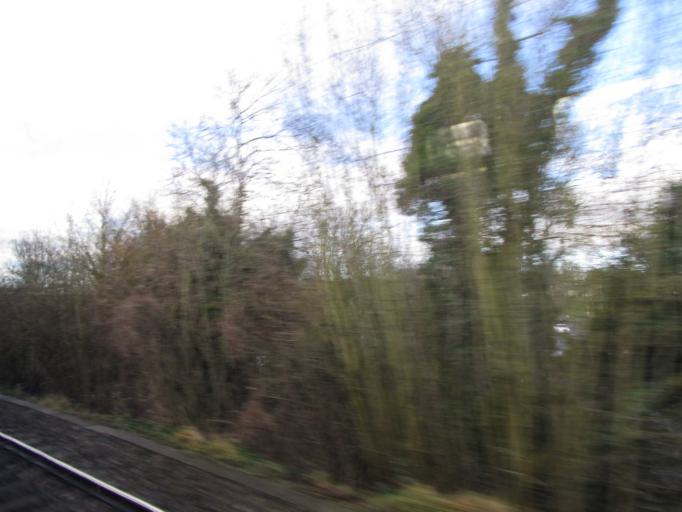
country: GB
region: England
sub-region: Hampshire
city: Basingstoke
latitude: 51.2856
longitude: -1.0687
